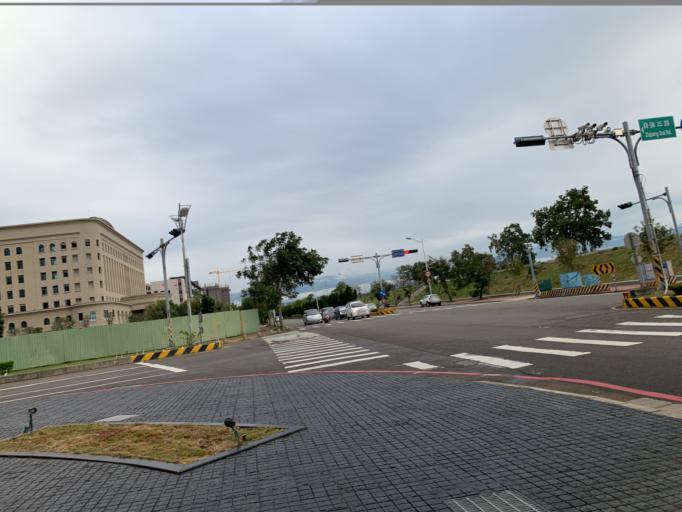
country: TW
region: Taiwan
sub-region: Hsinchu
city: Zhubei
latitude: 24.8145
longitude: 121.0161
